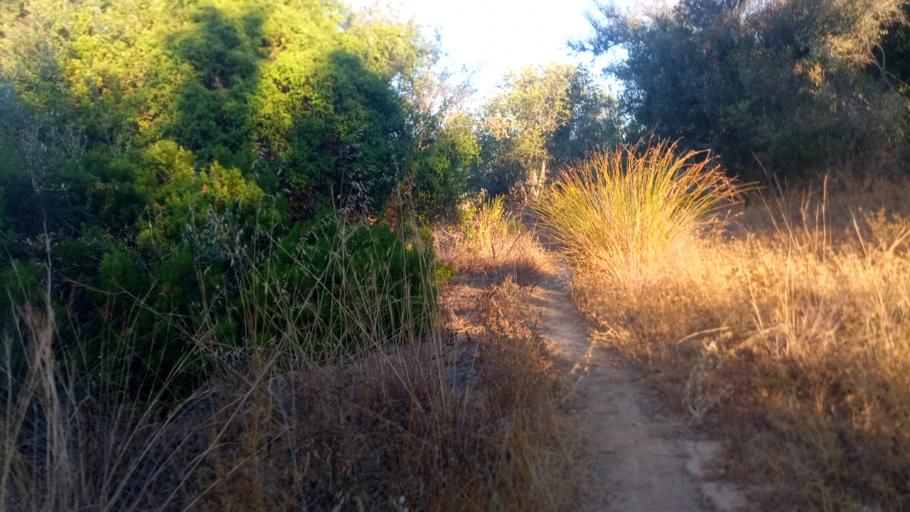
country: PT
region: Faro
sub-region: Tavira
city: Tavira
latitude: 37.1412
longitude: -7.6155
